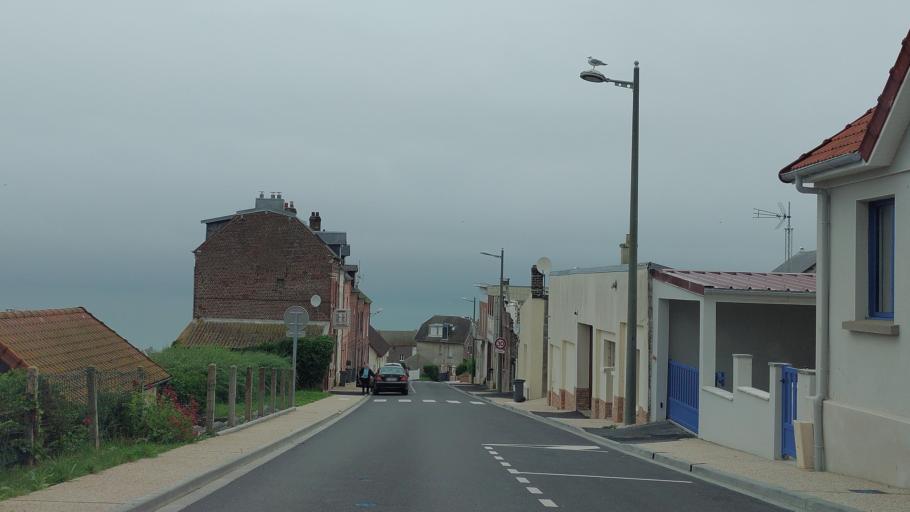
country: FR
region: Picardie
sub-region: Departement de la Somme
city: Ault
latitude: 50.1040
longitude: 1.4520
